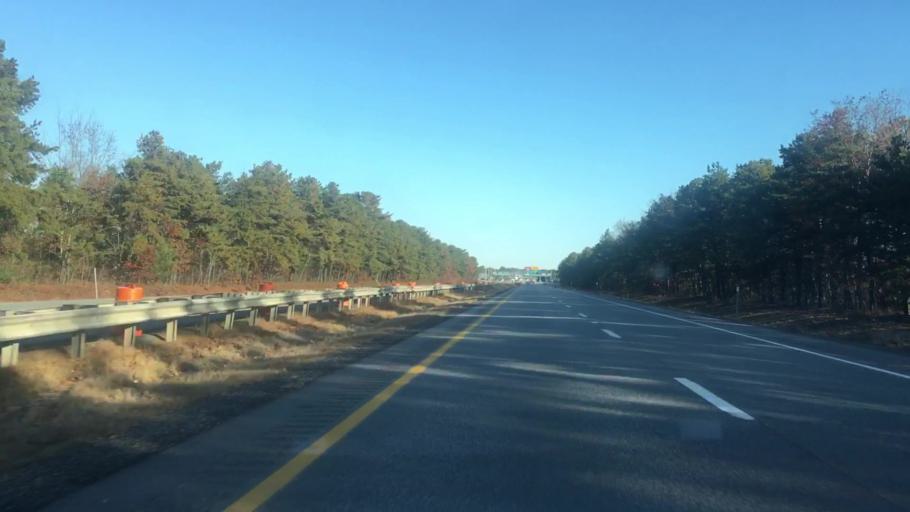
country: US
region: Maine
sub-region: Cumberland County
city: New Gloucester
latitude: 43.9283
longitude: -70.3363
